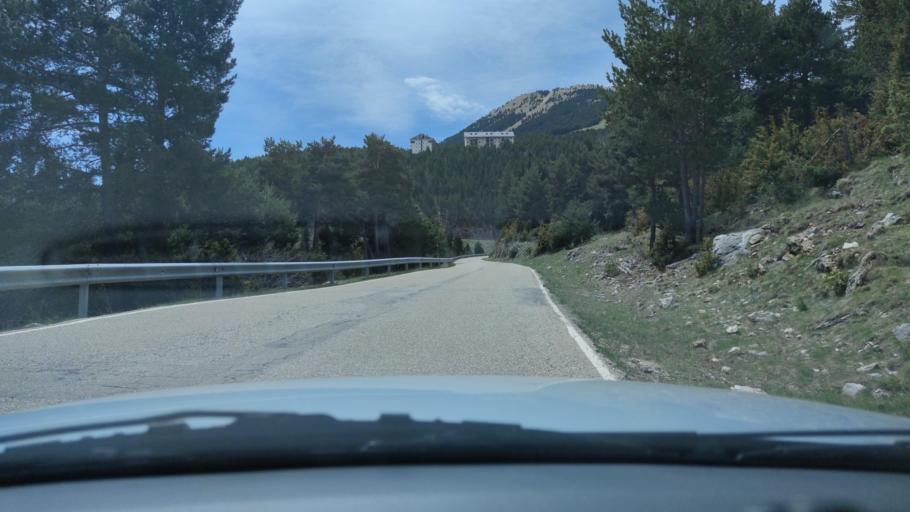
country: ES
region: Catalonia
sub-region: Provincia de Lleida
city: Gosol
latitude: 42.1787
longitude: 1.5587
